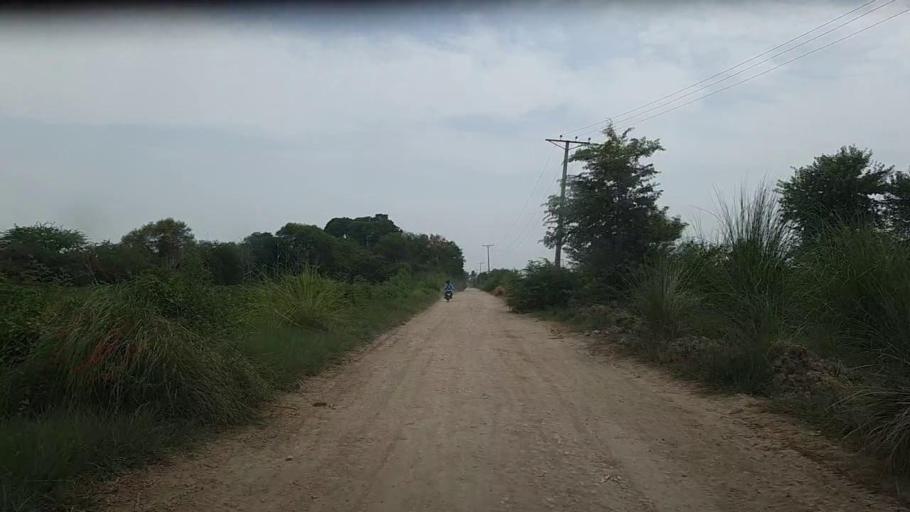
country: PK
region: Sindh
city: Bhiria
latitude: 26.8867
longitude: 68.2954
